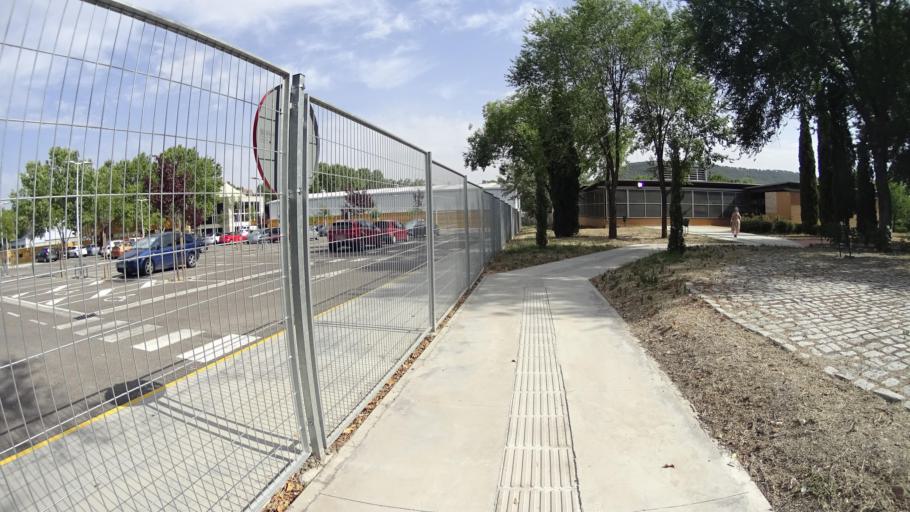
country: ES
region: Madrid
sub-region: Provincia de Madrid
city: Alcala de Henares
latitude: 40.4769
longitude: -3.3906
